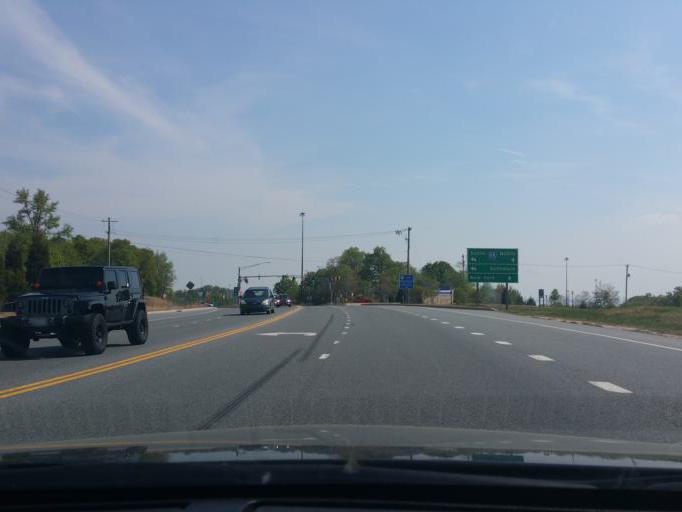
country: US
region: Maryland
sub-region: Cecil County
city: Perryville
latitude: 39.5975
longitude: -76.0677
